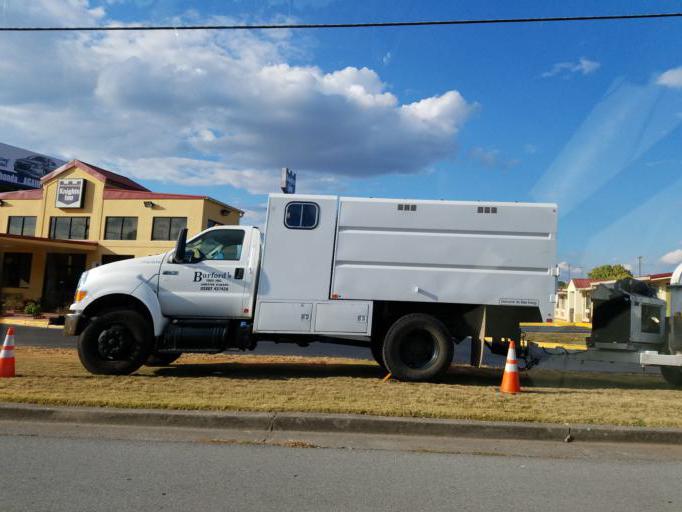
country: US
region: Georgia
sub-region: Bartow County
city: Cartersville
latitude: 34.1698
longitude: -84.7852
